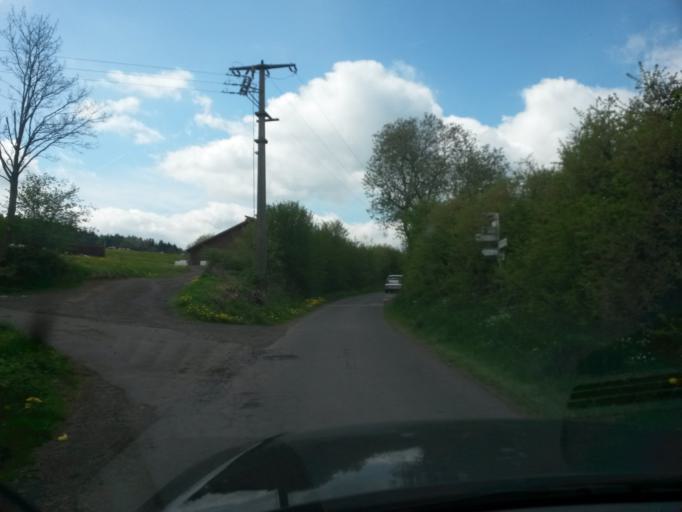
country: DE
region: Hesse
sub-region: Regierungsbezirk Kassel
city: Hilders
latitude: 50.5402
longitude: 9.9870
